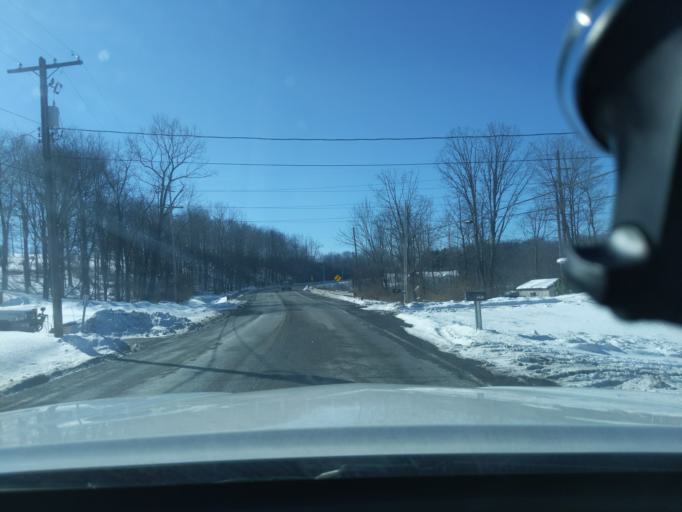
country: US
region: Maryland
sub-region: Allegany County
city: Frostburg
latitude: 39.6367
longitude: -78.9311
